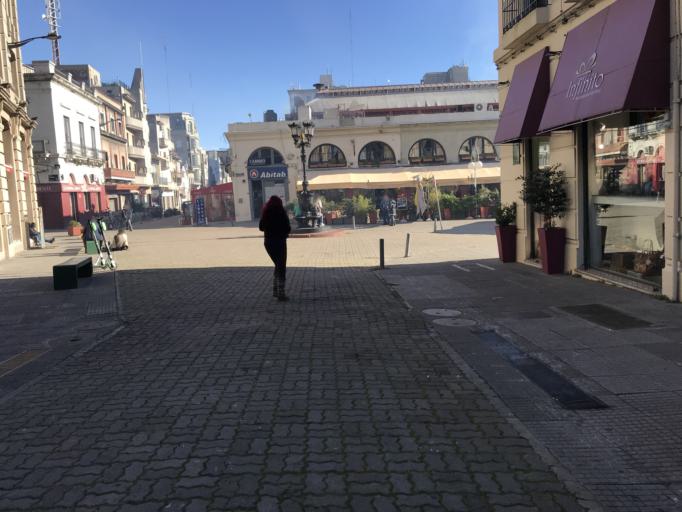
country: UY
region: Montevideo
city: Montevideo
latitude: -34.9056
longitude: -56.2110
